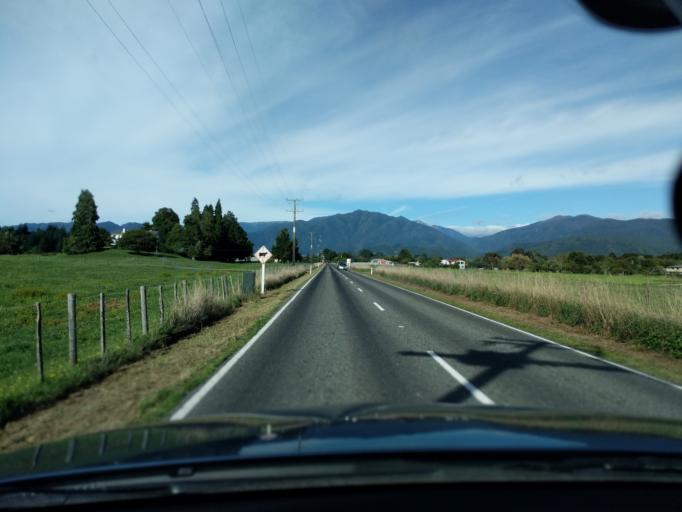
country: NZ
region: Tasman
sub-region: Tasman District
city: Takaka
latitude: -40.8526
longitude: 172.8285
